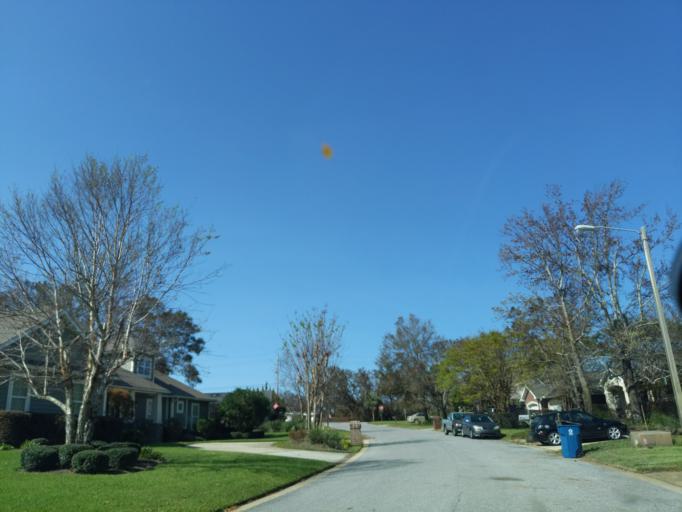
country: US
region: Florida
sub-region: Santa Rosa County
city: Gulf Breeze
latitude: 30.3513
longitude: -87.1862
